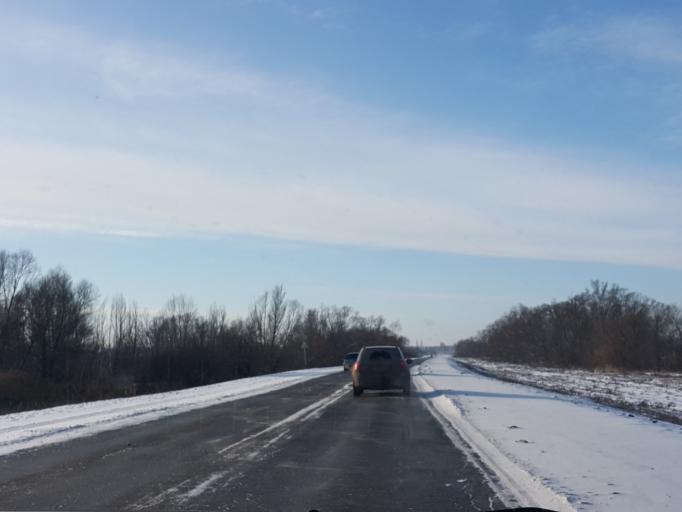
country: RU
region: Tambov
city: Znamenka
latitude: 52.4132
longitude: 41.4788
